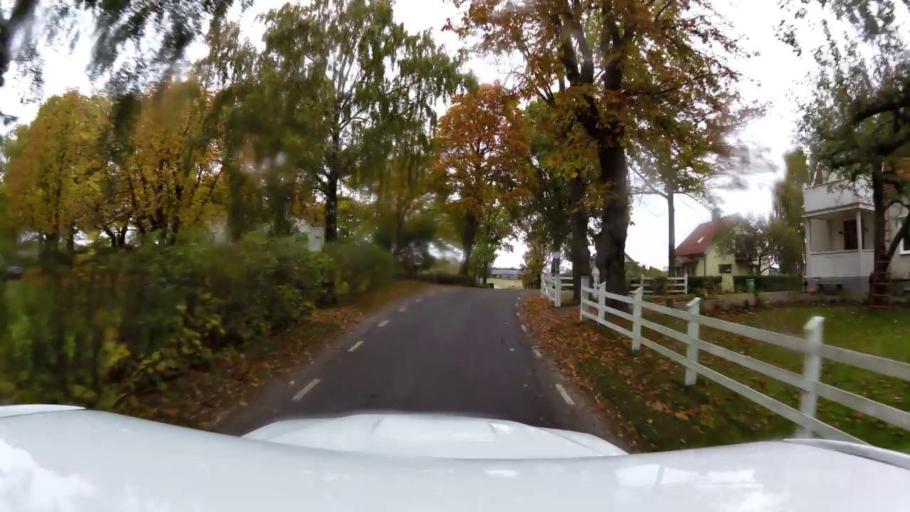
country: SE
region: OEstergoetland
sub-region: Linkopings Kommun
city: Linghem
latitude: 58.4521
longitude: 15.8331
